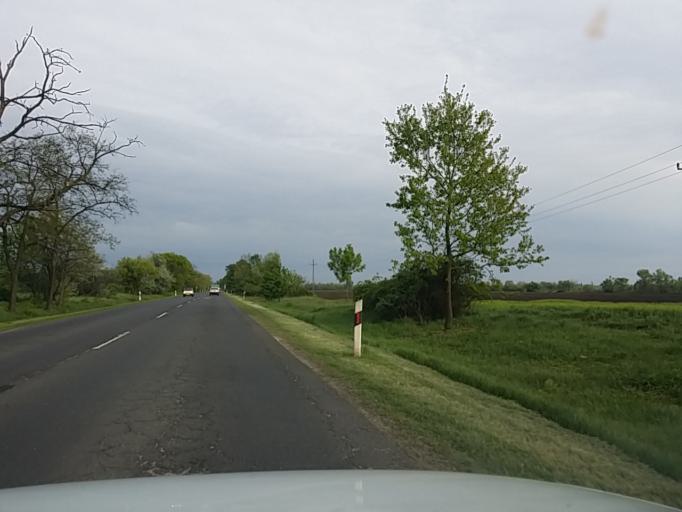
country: HU
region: Jasz-Nagykun-Szolnok
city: Jaszbereny
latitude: 47.5221
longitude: 19.8655
